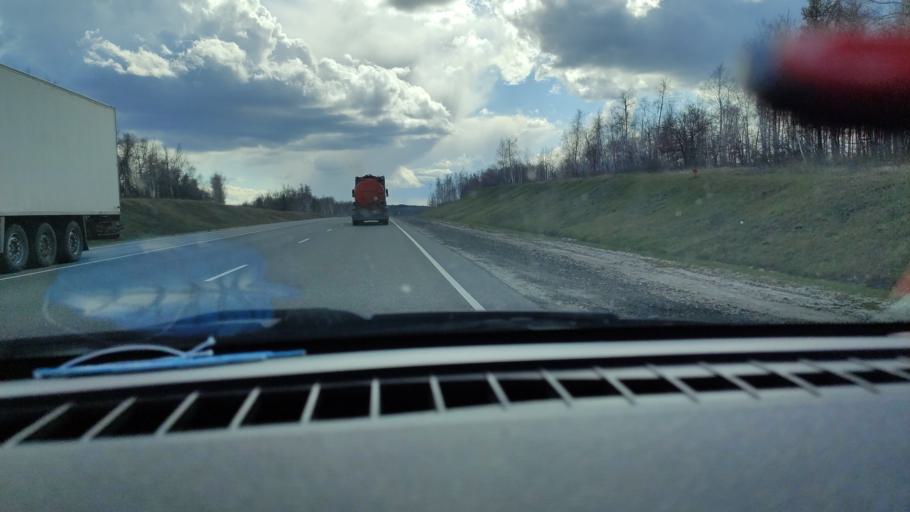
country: RU
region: Saratov
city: Khvalynsk
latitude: 52.5571
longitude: 48.0837
